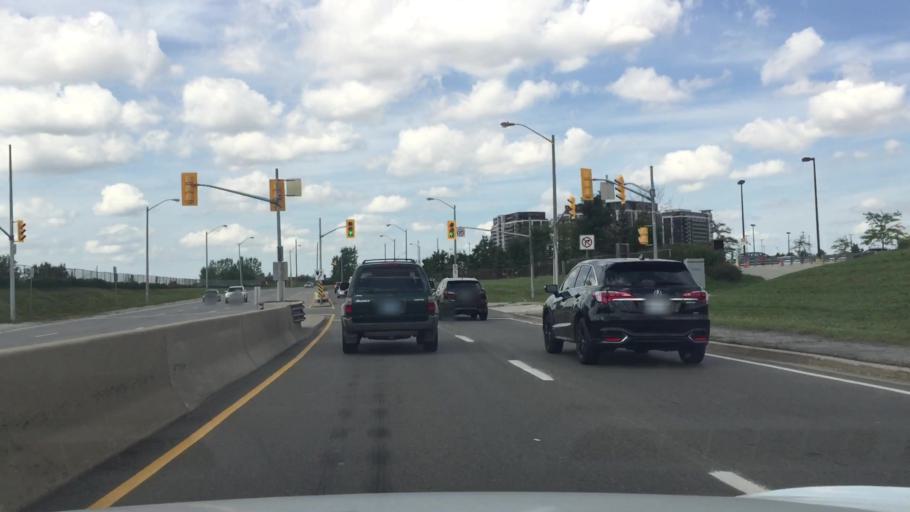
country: CA
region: Ontario
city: North York
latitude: 43.7464
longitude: -79.4597
